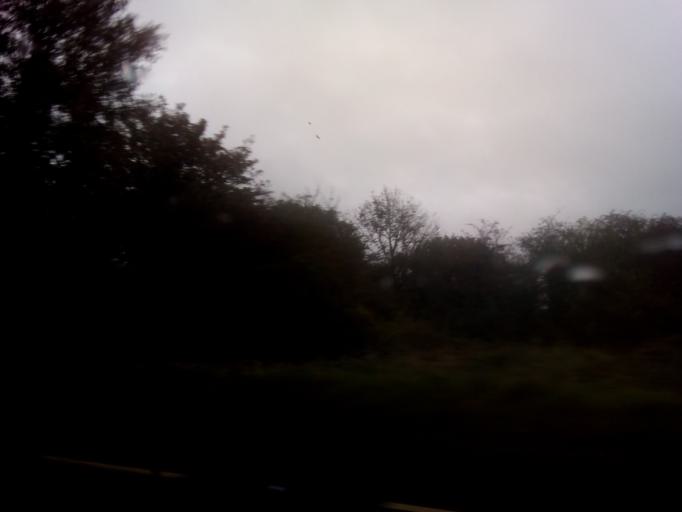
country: IE
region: Connaught
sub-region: Roscommon
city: Castlerea
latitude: 53.8637
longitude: -8.4014
